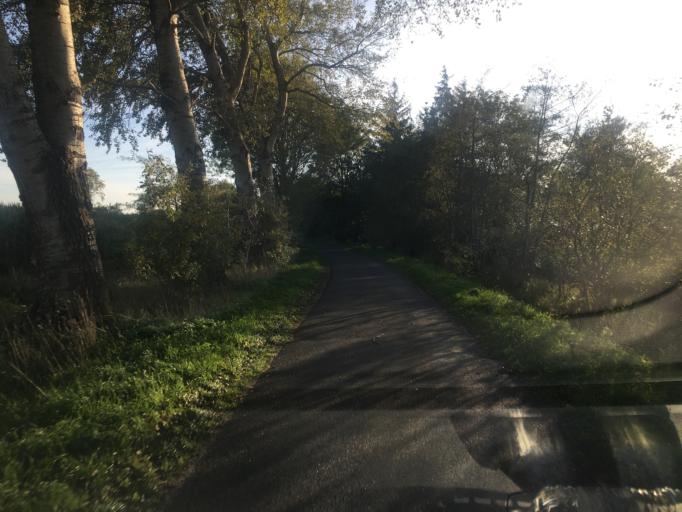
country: DE
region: Schleswig-Holstein
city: Bramstedtlund
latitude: 54.8581
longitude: 9.0758
